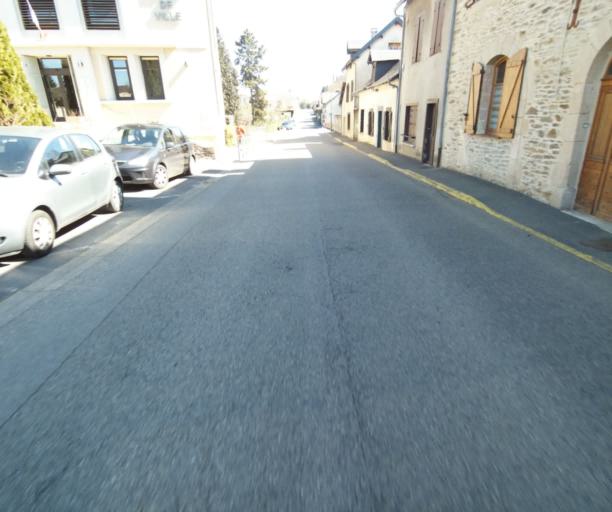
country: FR
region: Limousin
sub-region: Departement de la Correze
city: Seilhac
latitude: 45.3673
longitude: 1.7138
